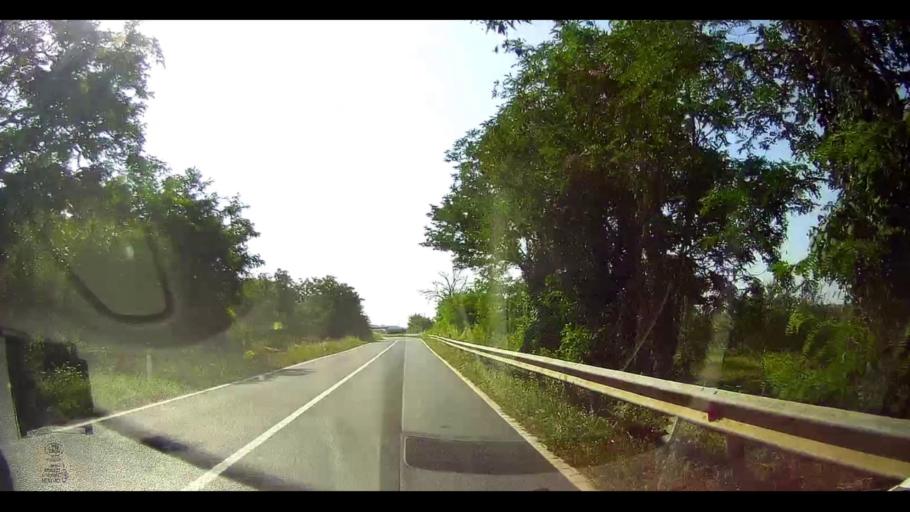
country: IT
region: Calabria
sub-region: Provincia di Crotone
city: Torretta
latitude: 39.4777
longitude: 16.9993
